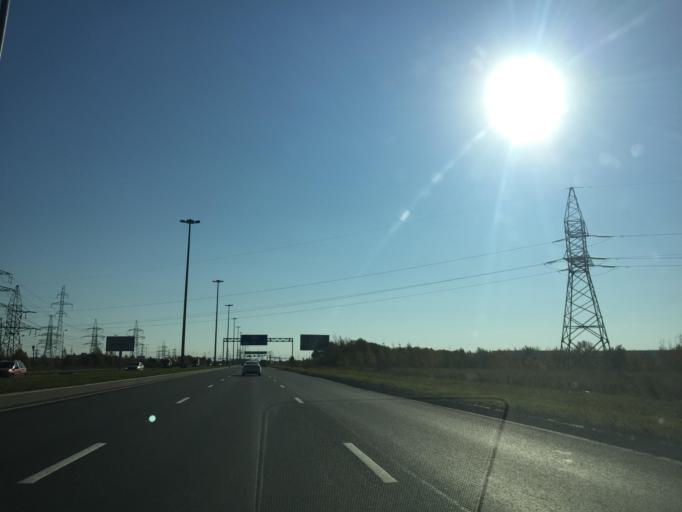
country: RU
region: St.-Petersburg
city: Petro-Slavyanka
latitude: 59.7529
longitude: 30.5240
